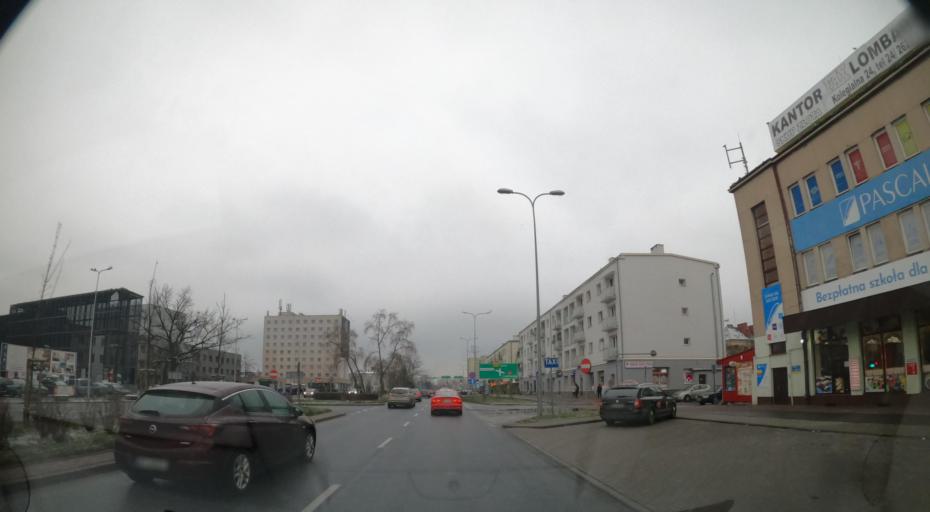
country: PL
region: Masovian Voivodeship
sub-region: Plock
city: Plock
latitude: 52.5493
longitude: 19.6938
